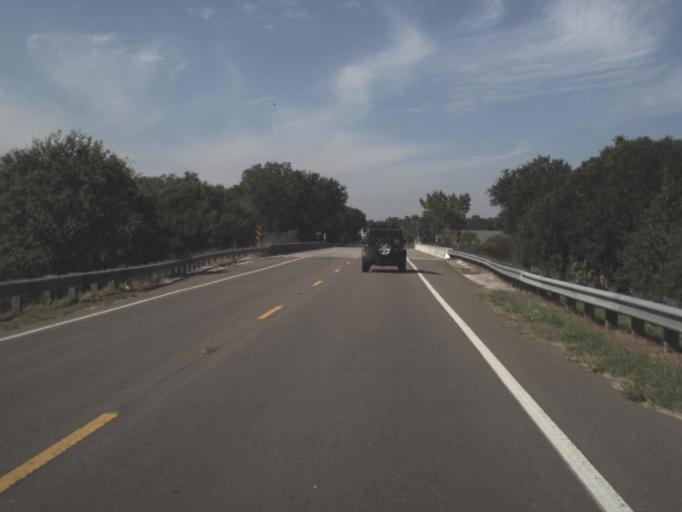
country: US
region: Florida
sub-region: Hardee County
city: Wauchula
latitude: 27.5508
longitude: -81.7925
